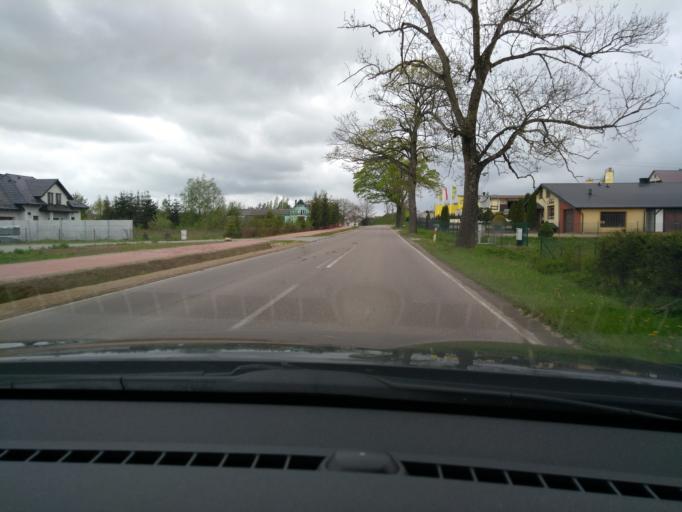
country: PL
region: Pomeranian Voivodeship
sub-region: Powiat kartuski
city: Sierakowice
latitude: 54.3402
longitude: 17.9176
